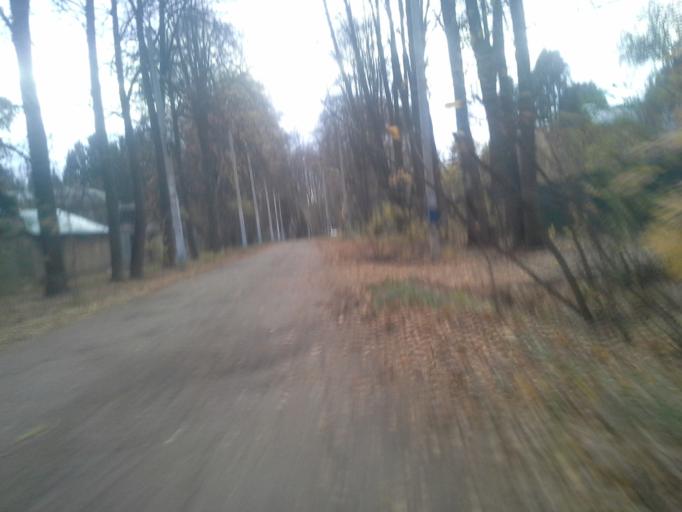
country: RU
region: Moscow
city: Novo-Peredelkino
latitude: 55.6487
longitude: 37.3255
